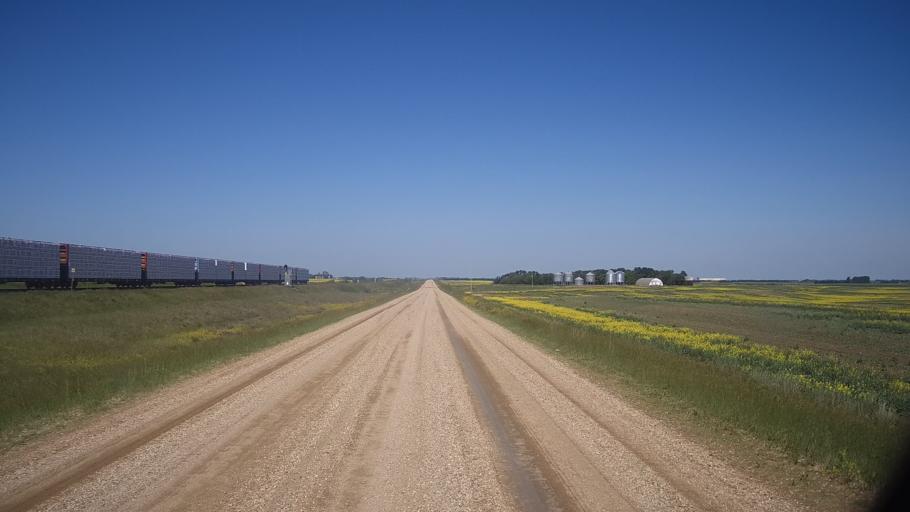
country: CA
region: Saskatchewan
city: Watrous
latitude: 51.8612
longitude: -105.9653
